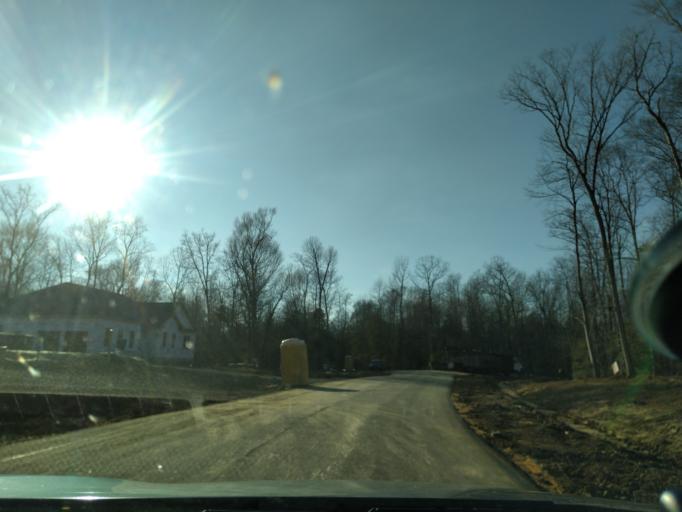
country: US
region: Maryland
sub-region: Charles County
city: La Plata
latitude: 38.4917
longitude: -76.8929
